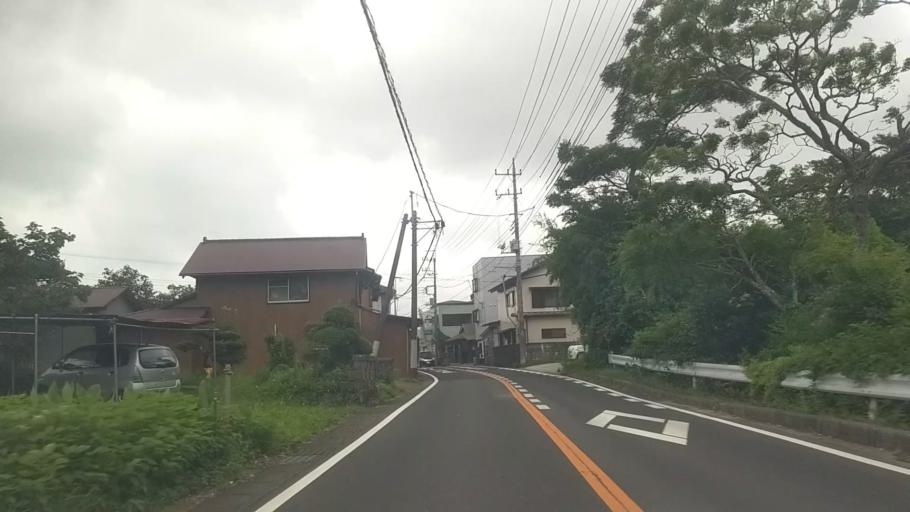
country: JP
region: Chiba
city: Katsuura
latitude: 35.2517
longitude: 140.1972
